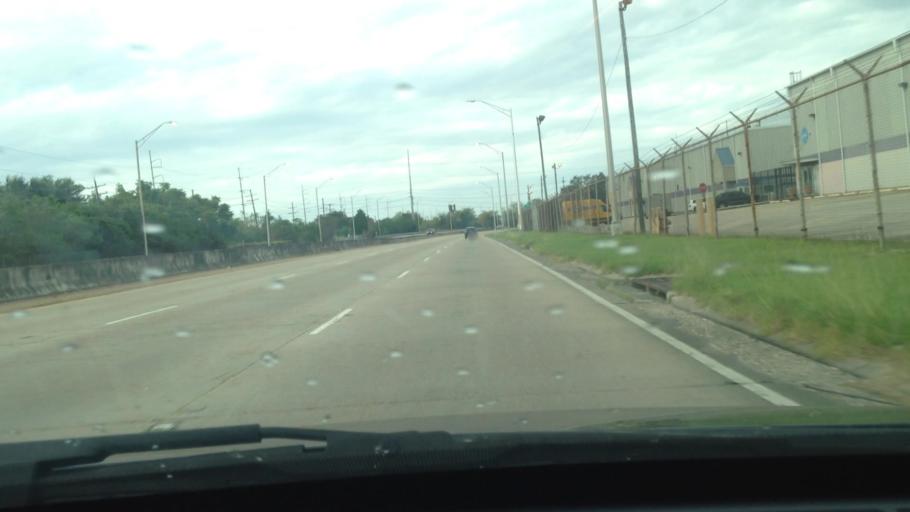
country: US
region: Louisiana
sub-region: Jefferson Parish
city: Jefferson
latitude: 29.9702
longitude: -90.1485
